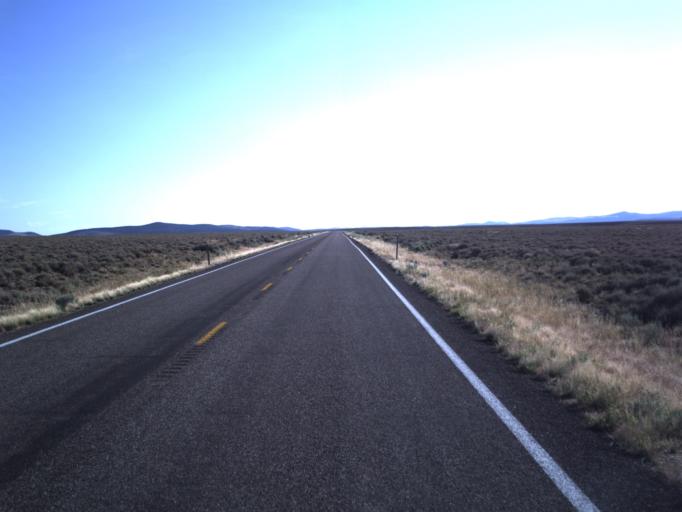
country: US
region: Utah
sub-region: Iron County
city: Enoch
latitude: 37.9500
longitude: -113.0157
